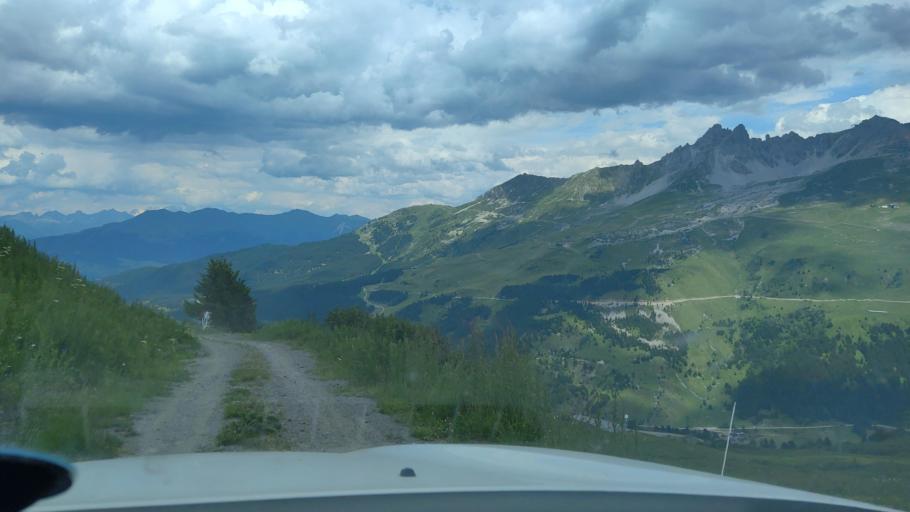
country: FR
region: Rhone-Alpes
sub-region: Departement de la Savoie
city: Meribel
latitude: 45.3741
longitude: 6.5567
